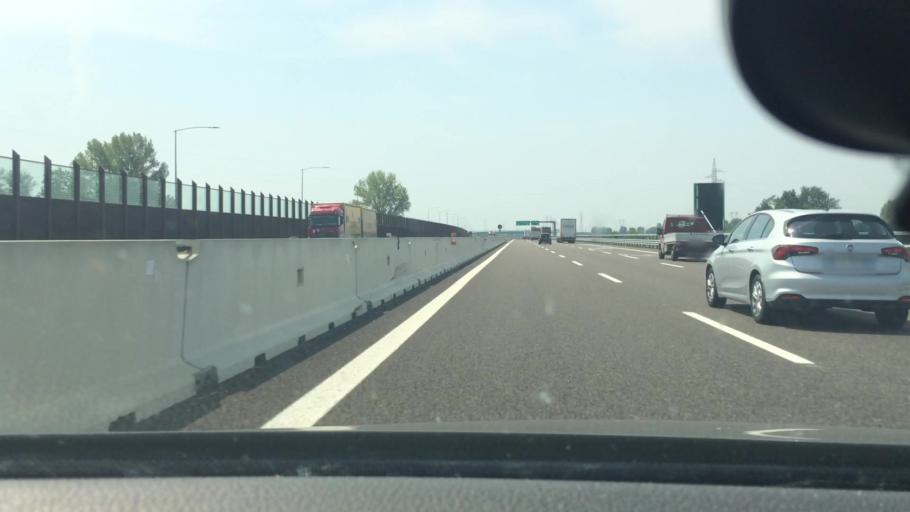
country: IT
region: Lombardy
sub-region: Provincia di Lodi
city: Merlino
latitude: 45.4378
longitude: 9.4248
